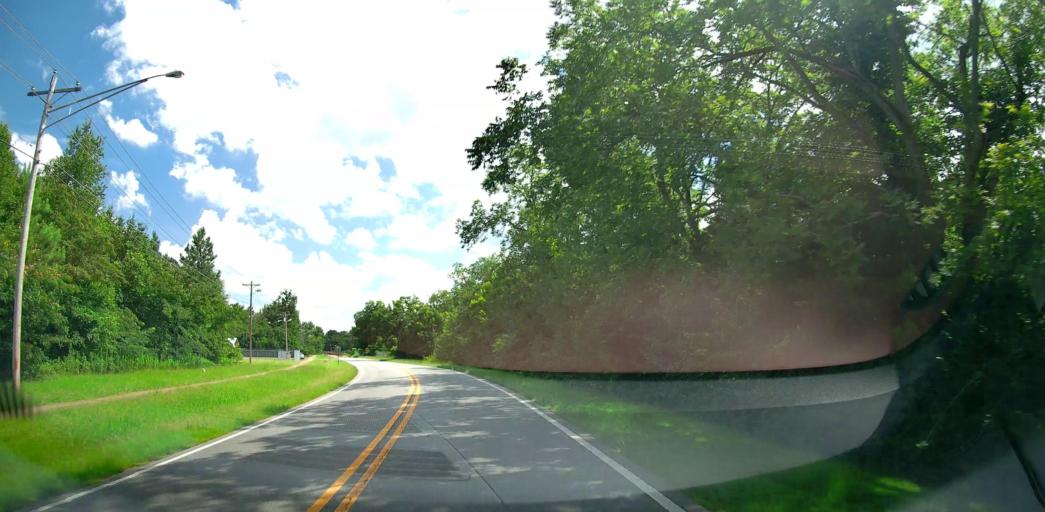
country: US
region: Georgia
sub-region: Houston County
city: Warner Robins
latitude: 32.6473
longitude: -83.6289
